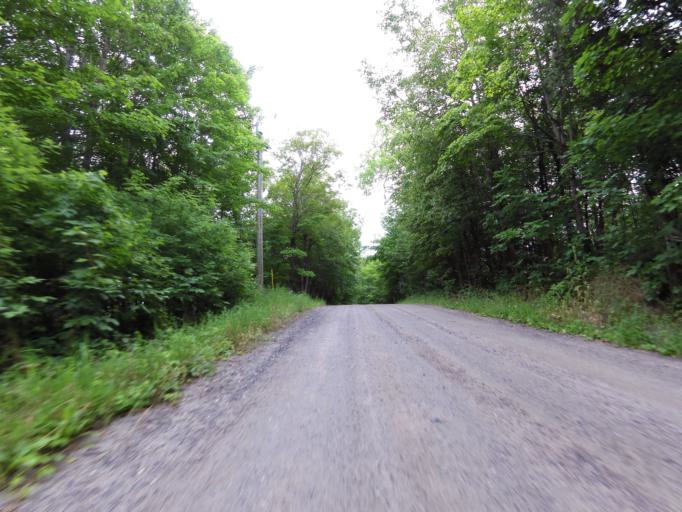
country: CA
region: Ontario
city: Perth
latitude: 45.0478
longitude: -76.3955
